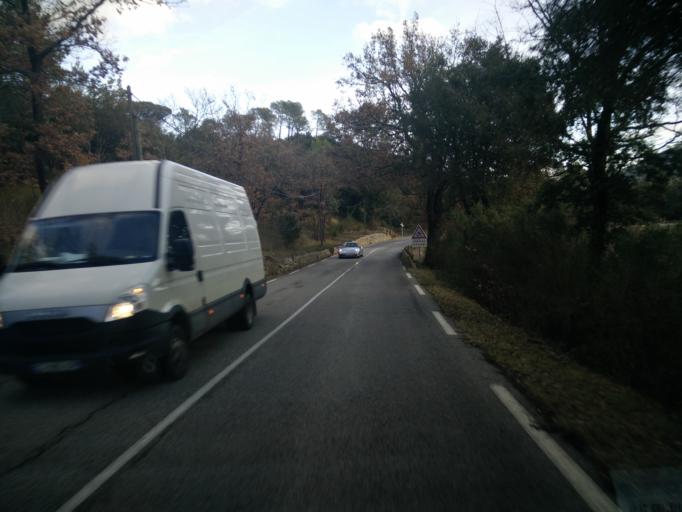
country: FR
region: Provence-Alpes-Cote d'Azur
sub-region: Departement du Var
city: Signes
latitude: 43.2797
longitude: 5.9074
